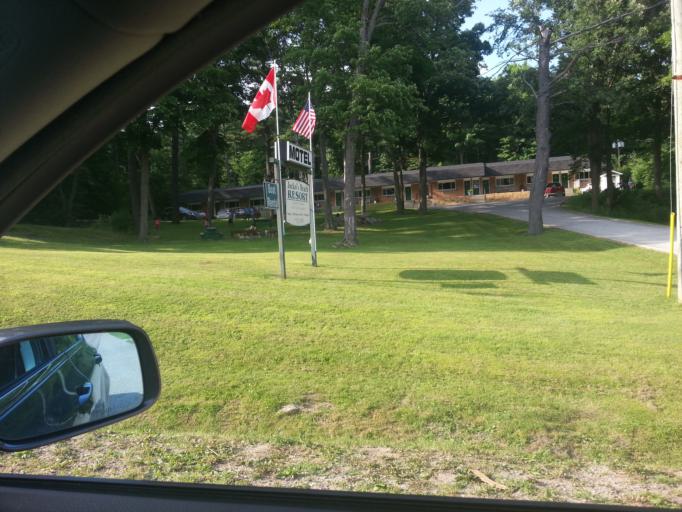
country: CA
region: Ontario
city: Renfrew
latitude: 45.2942
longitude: -76.7450
